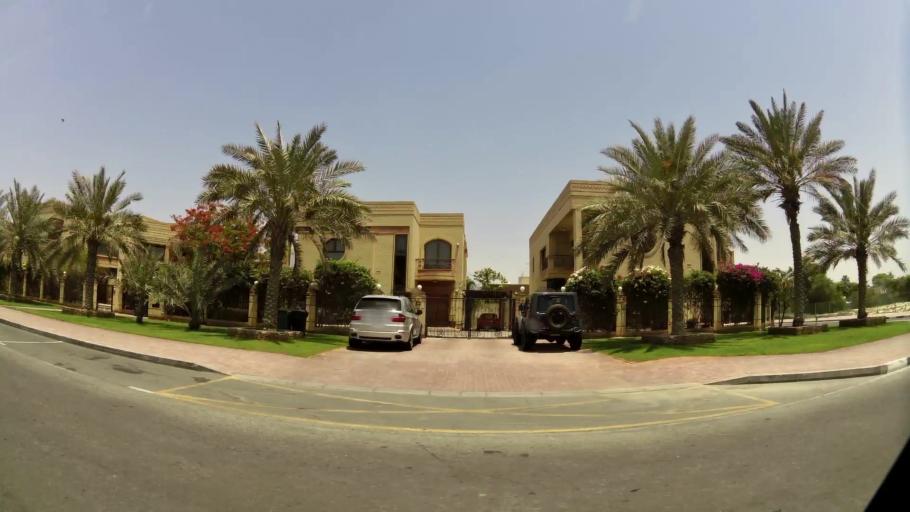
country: AE
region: Dubai
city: Dubai
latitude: 25.2017
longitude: 55.2436
